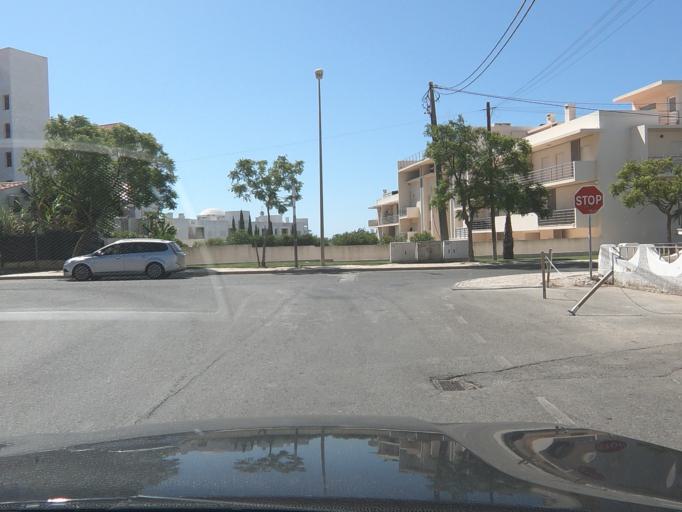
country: PT
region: Faro
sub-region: Albufeira
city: Albufeira
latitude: 37.1033
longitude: -8.2353
